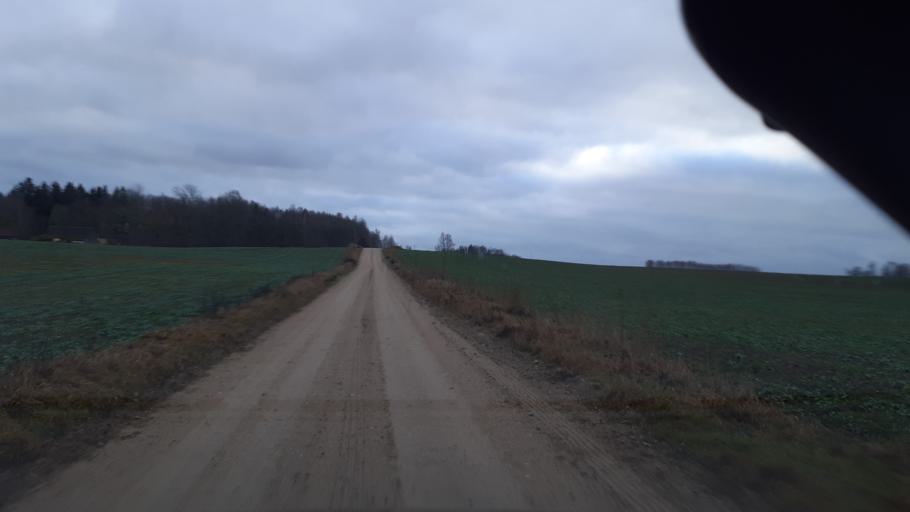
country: LV
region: Kuldigas Rajons
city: Kuldiga
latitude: 56.8643
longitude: 21.7709
